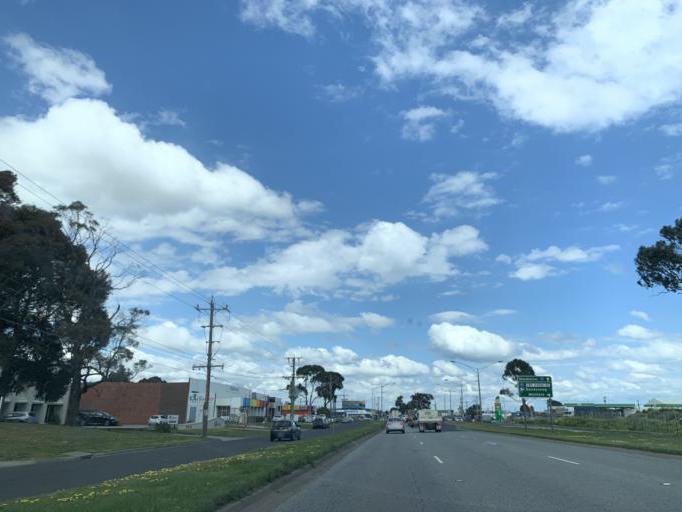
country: AU
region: Victoria
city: Heatherton
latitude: -37.9844
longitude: 145.1099
